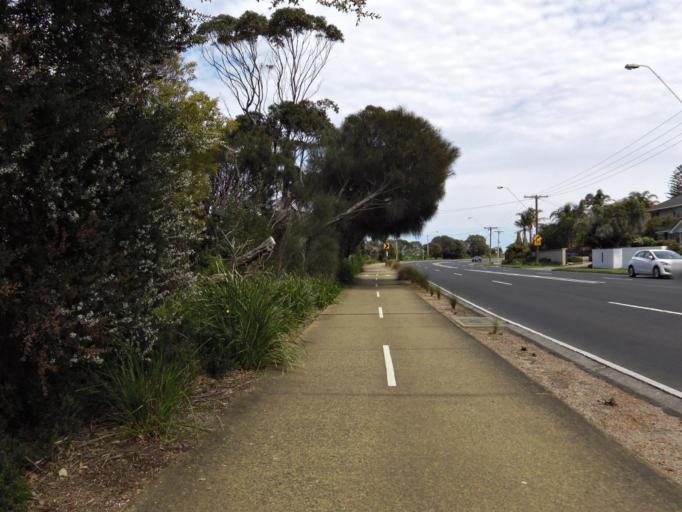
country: AU
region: Victoria
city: Beaumaris
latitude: -37.9946
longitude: 145.0392
